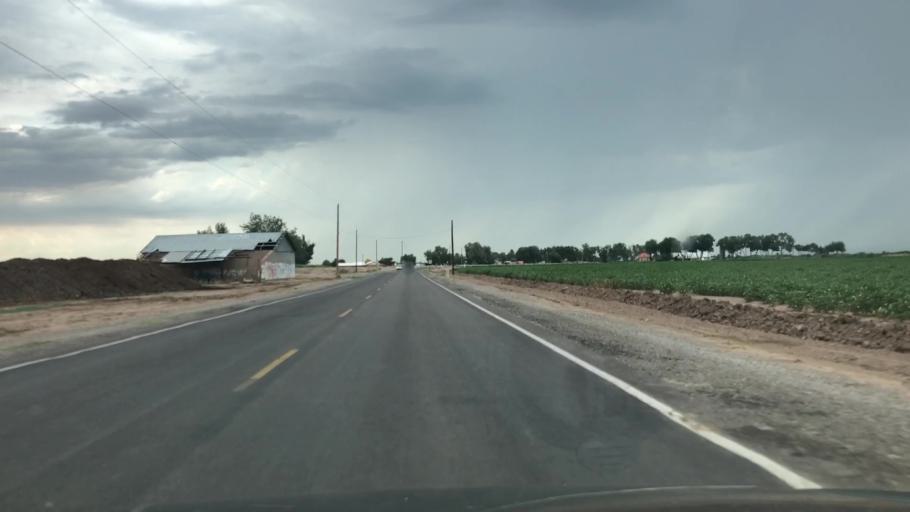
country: US
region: New Mexico
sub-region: Dona Ana County
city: Anthony
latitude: 32.0230
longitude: -106.6707
